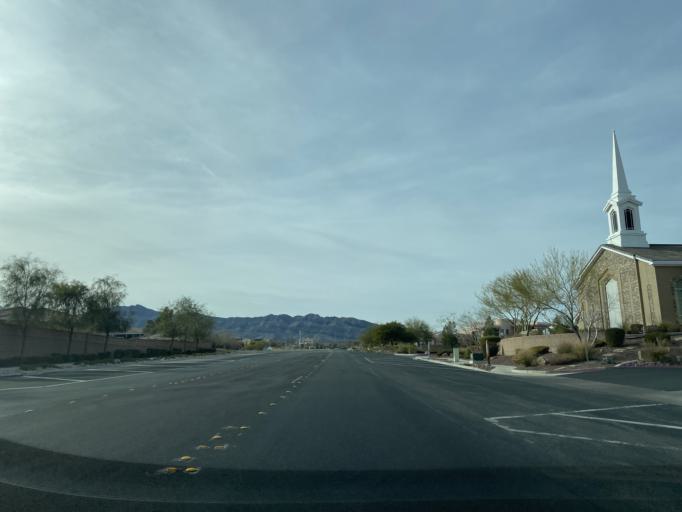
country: US
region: Nevada
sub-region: Clark County
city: Summerlin South
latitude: 36.2921
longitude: -115.3104
